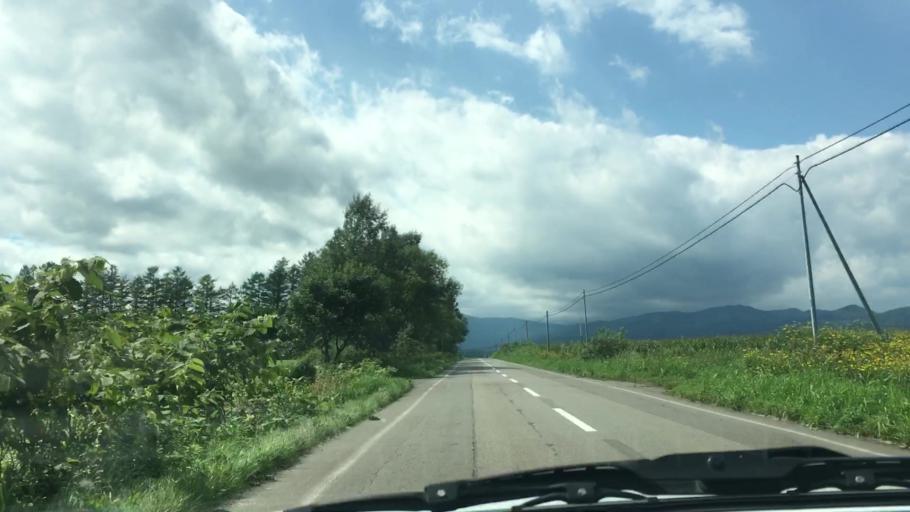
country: JP
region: Hokkaido
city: Otofuke
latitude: 43.2793
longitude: 143.3474
